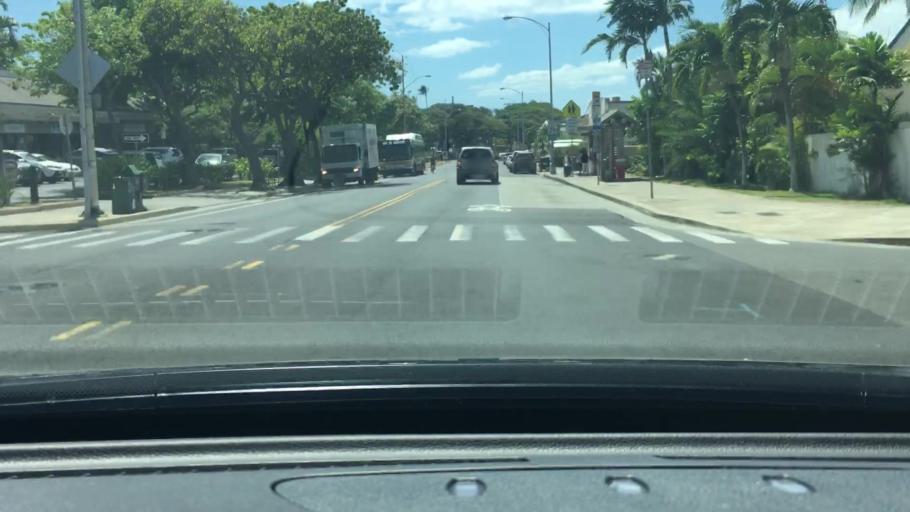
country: US
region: Hawaii
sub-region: Honolulu County
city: Honolulu
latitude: 21.2691
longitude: -157.8132
